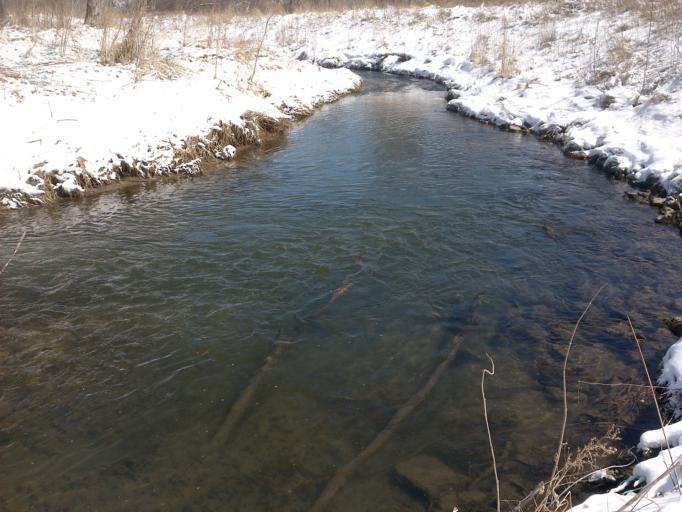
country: US
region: Minnesota
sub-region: Goodhue County
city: Goodhue
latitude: 44.4787
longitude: -92.5861
